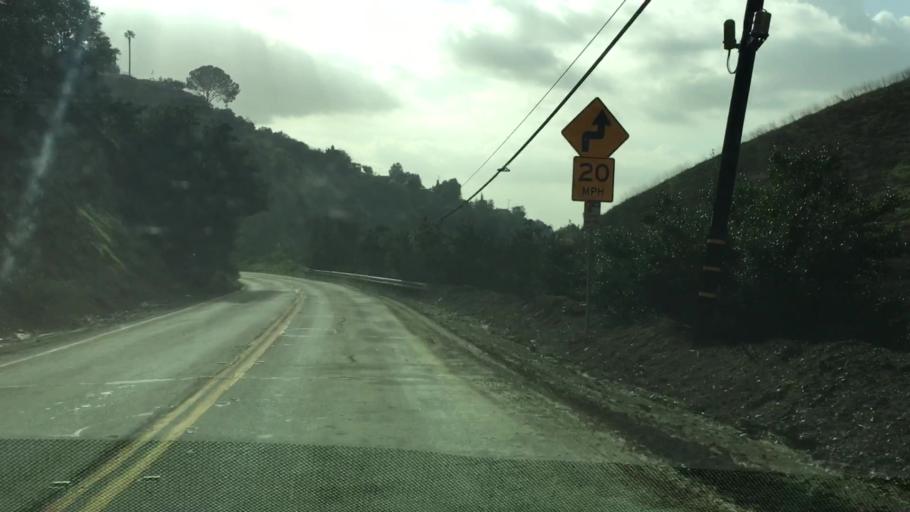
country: US
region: California
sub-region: Los Angeles County
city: Whittier
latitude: 33.9898
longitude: -118.0212
